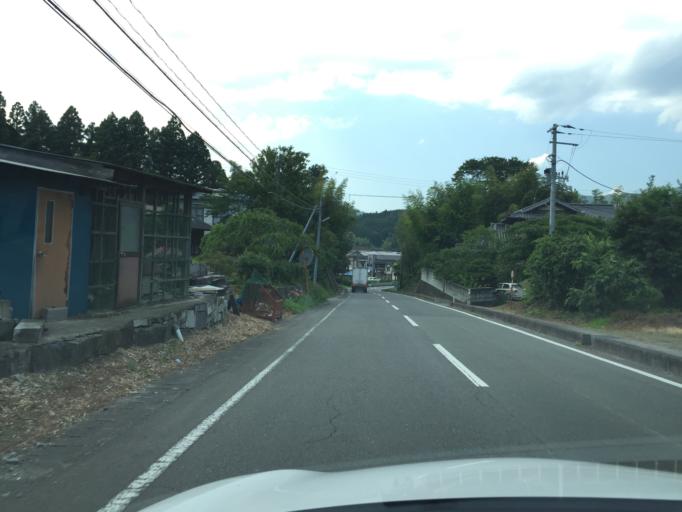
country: JP
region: Fukushima
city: Iwaki
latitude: 37.0332
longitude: 140.7102
